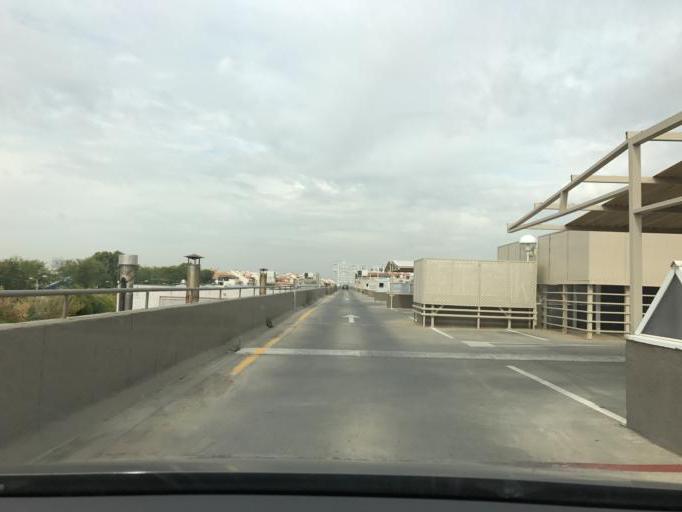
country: ES
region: Andalusia
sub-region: Provincia de Granada
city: Armilla
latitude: 37.1539
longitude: -3.6080
